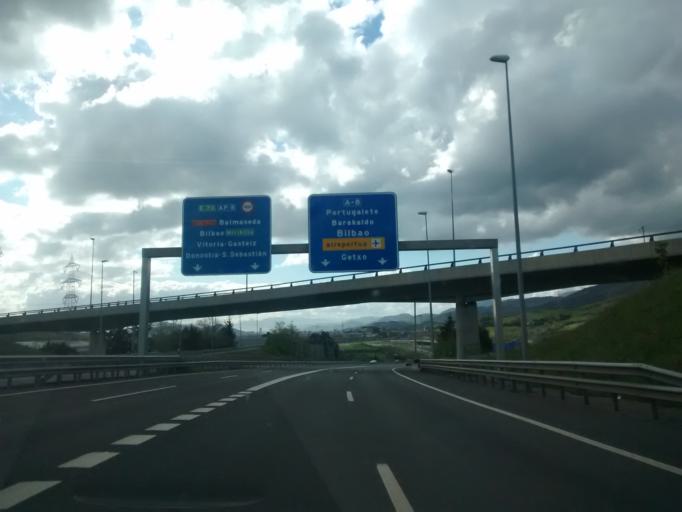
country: ES
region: Basque Country
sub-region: Bizkaia
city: Urtuella
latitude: 43.3218
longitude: -3.0539
